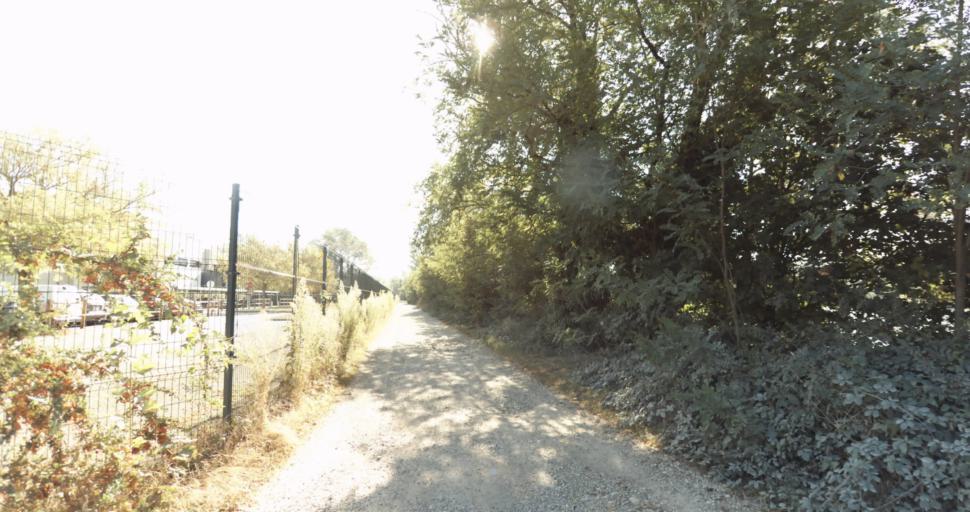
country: FR
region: Rhone-Alpes
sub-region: Departement du Rhone
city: Albigny-sur-Saone
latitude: 45.8816
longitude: 4.8244
